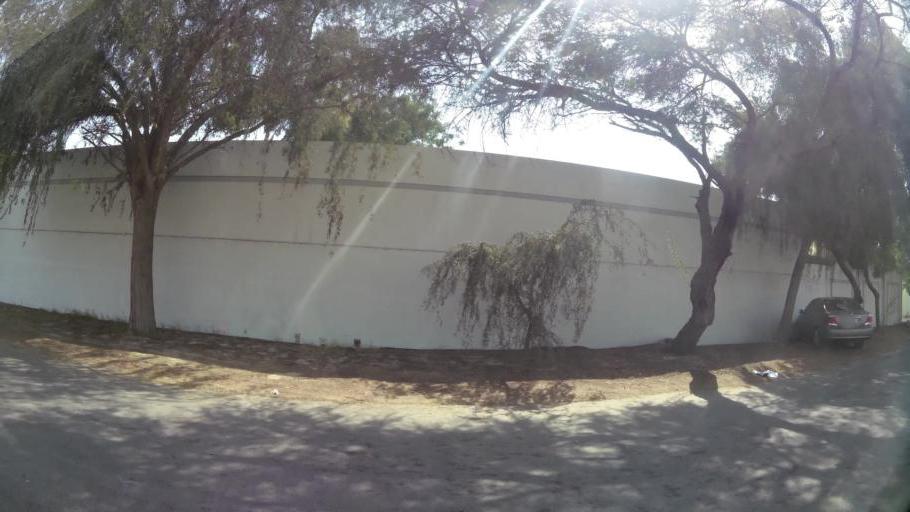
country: AE
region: Ajman
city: Ajman
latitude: 25.3834
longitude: 55.4185
